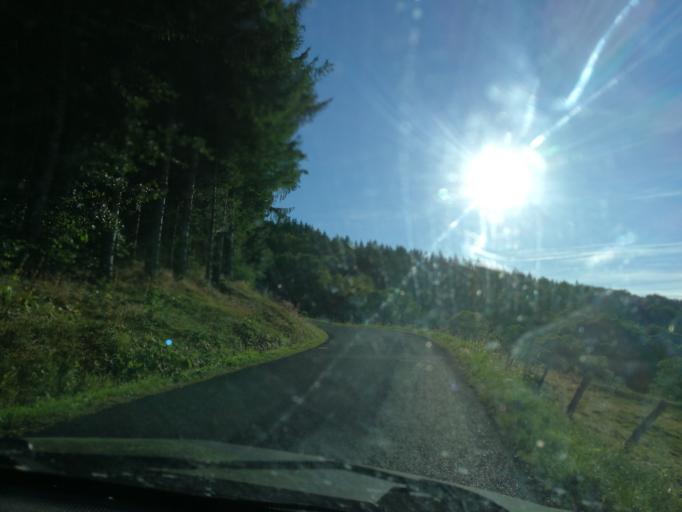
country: FR
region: Auvergne
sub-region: Departement du Cantal
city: Vic-sur-Cere
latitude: 45.0782
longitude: 2.5646
